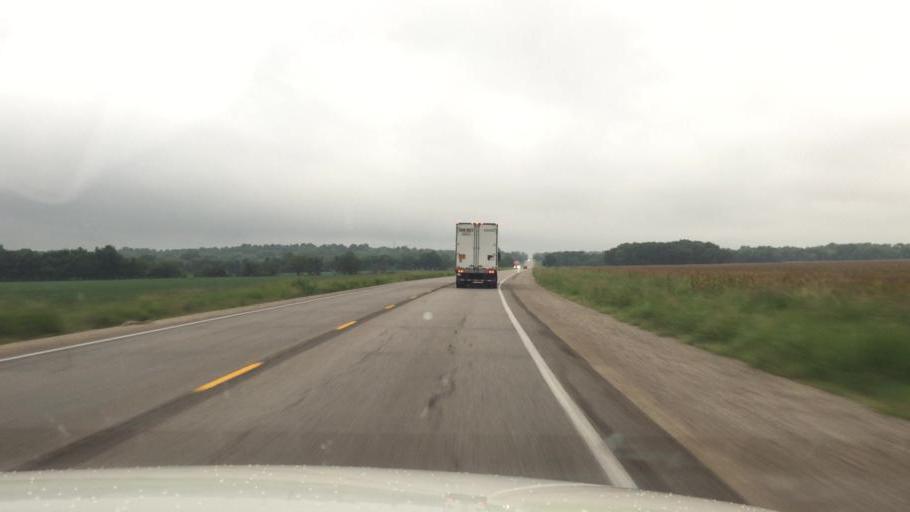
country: US
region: Kansas
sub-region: Montgomery County
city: Cherryvale
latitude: 37.1758
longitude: -95.5765
